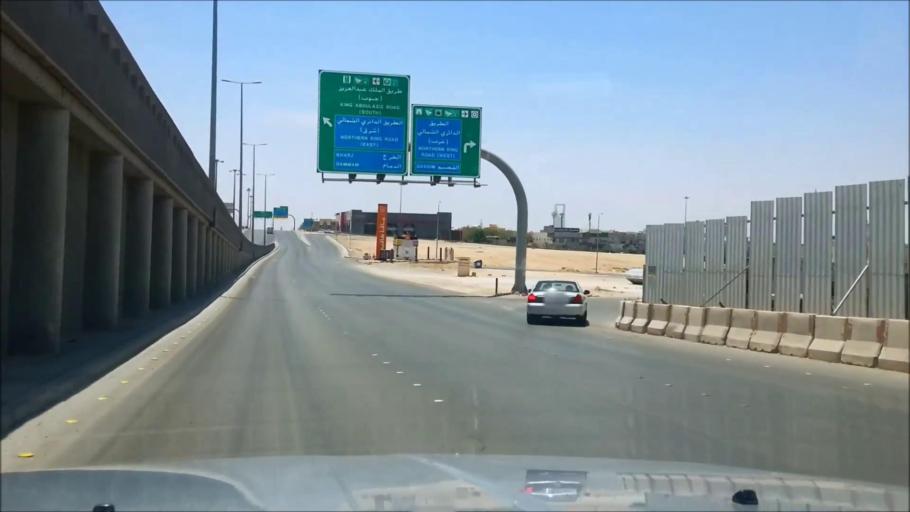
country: SA
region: Ar Riyad
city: Riyadh
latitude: 24.7729
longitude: 46.6667
